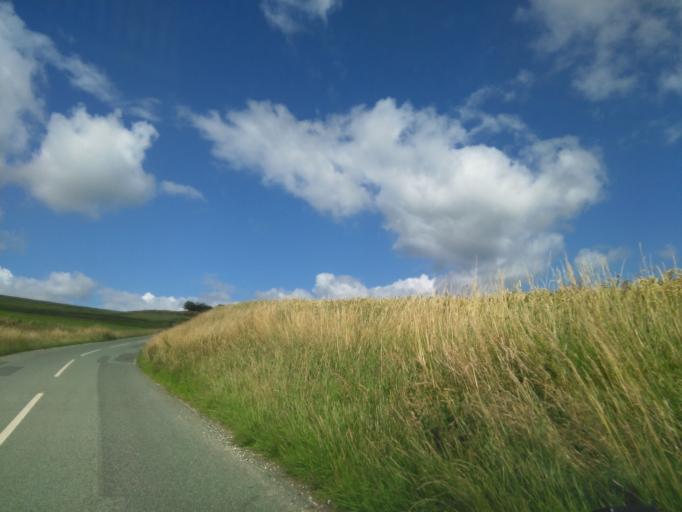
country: DK
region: Central Jutland
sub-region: Syddjurs Kommune
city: Ronde
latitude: 56.2196
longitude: 10.5049
